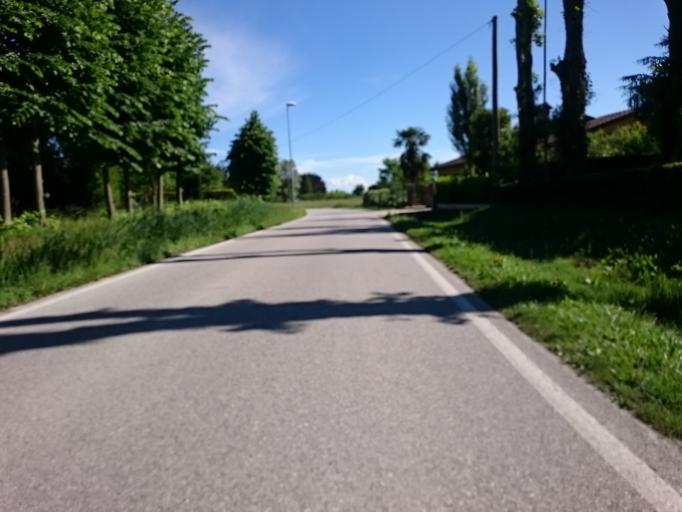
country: IT
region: Veneto
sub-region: Provincia di Padova
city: Legnaro
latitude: 45.3556
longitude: 11.9725
